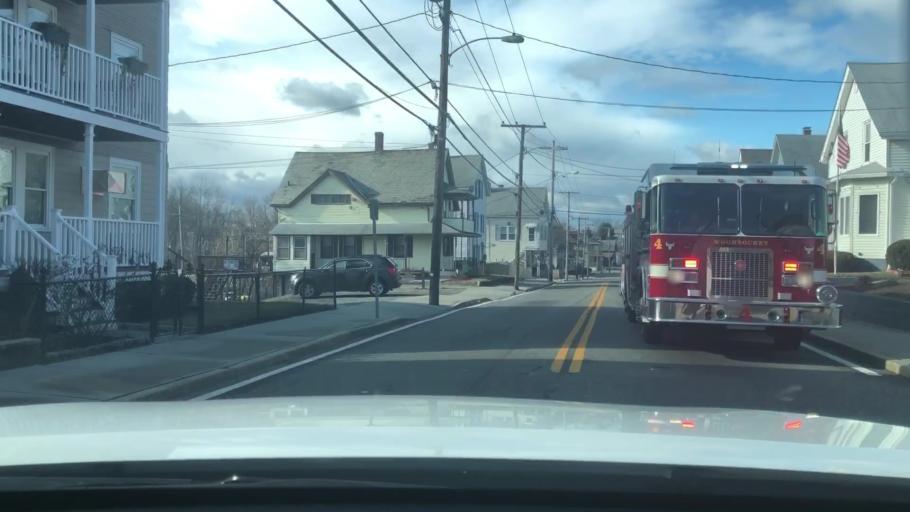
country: US
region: Rhode Island
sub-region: Providence County
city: Woonsocket
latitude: 42.0155
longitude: -71.4943
